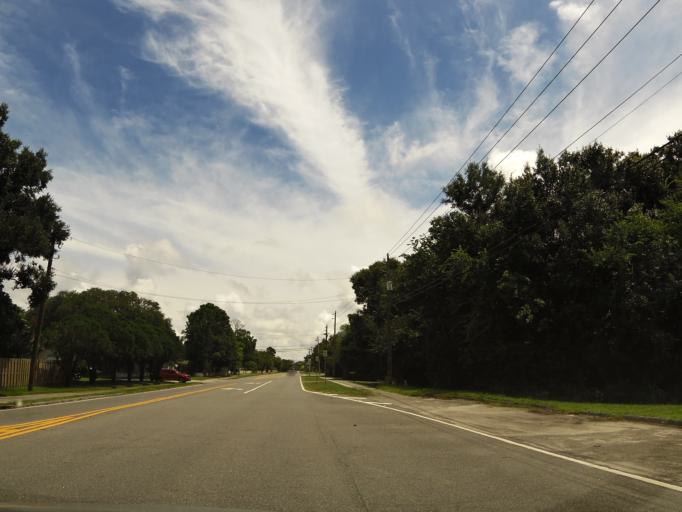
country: US
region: Florida
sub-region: Brevard County
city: Mims
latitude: 28.6372
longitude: -80.8535
